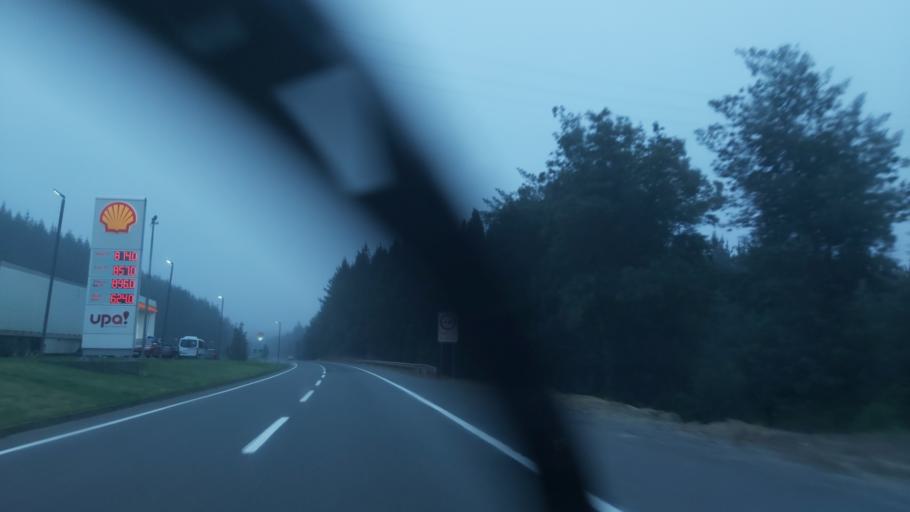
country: CL
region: Biobio
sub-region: Provincia de Concepcion
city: Penco
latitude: -36.7463
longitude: -72.9184
